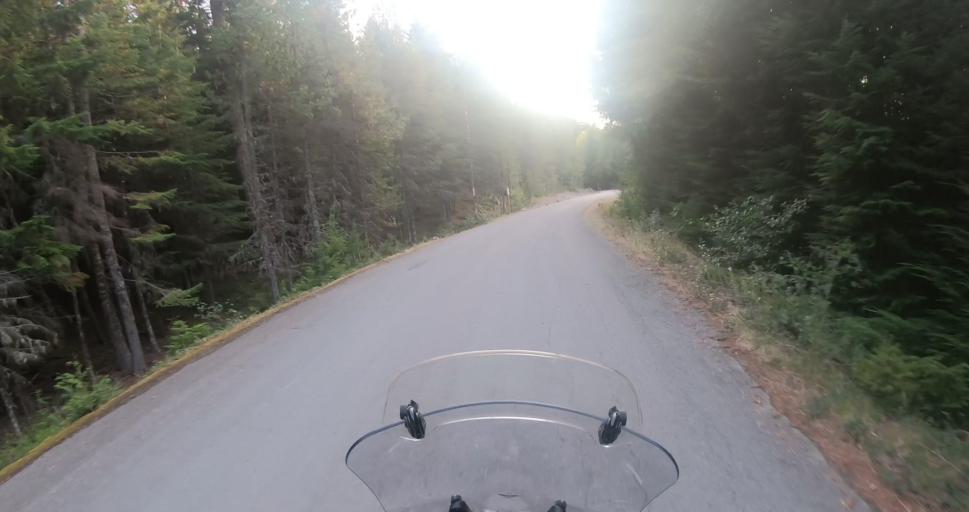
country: US
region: Oregon
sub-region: Hood River County
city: Odell
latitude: 45.4579
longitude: -121.6552
